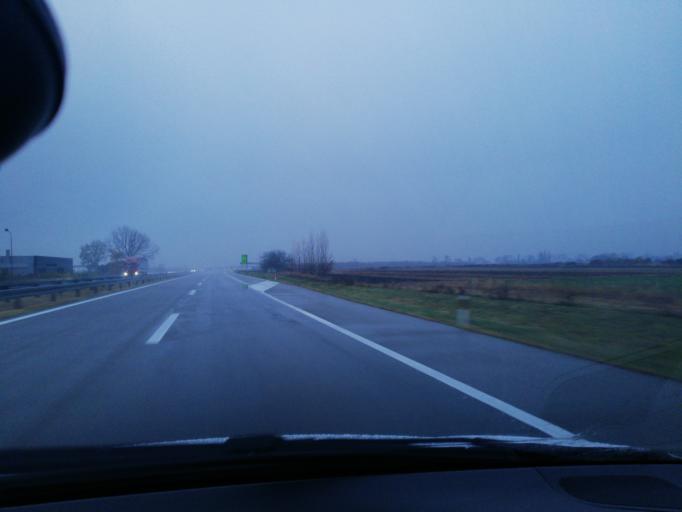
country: RS
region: Autonomna Pokrajina Vojvodina
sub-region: Sremski Okrug
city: Sremska Mitrovica
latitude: 45.0015
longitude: 19.6258
